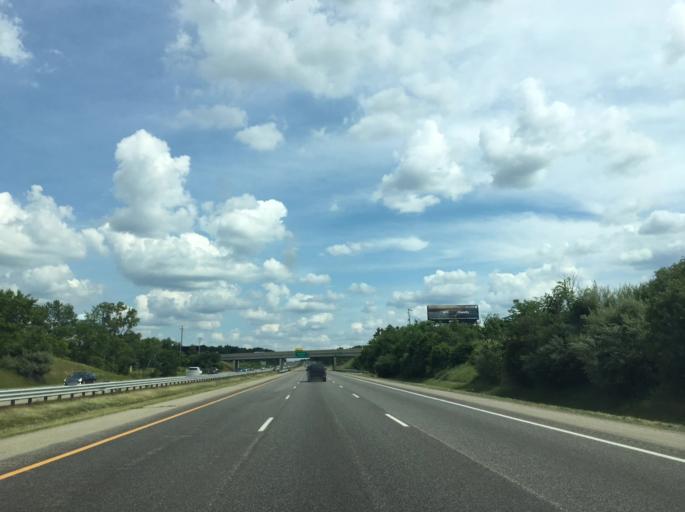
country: US
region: Michigan
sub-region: Genesee County
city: Grand Blanc
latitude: 42.8885
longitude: -83.6229
